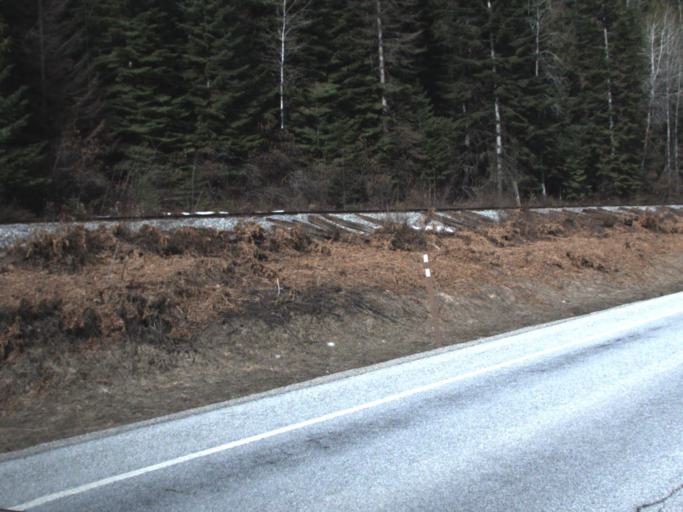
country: US
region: Washington
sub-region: Pend Oreille County
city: Newport
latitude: 48.2381
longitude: -117.2279
